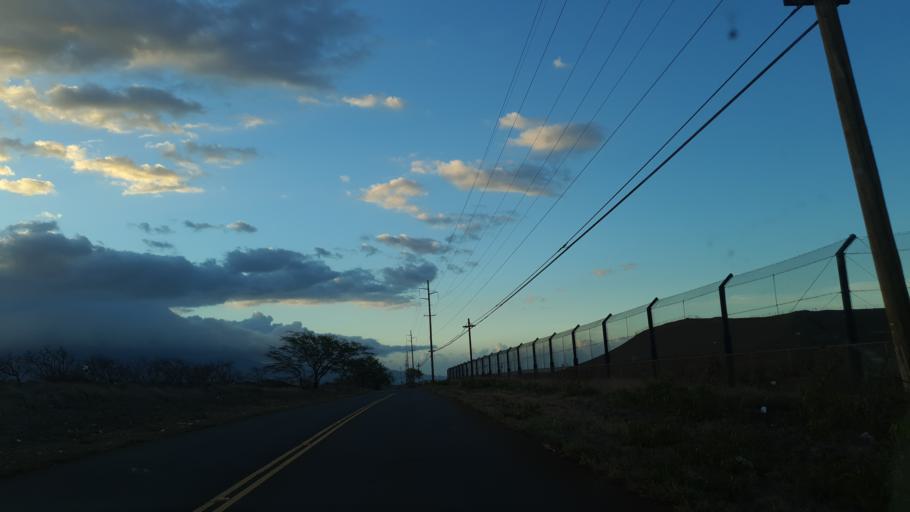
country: US
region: Hawaii
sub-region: Maui County
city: Kahului
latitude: 20.8548
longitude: -156.4214
